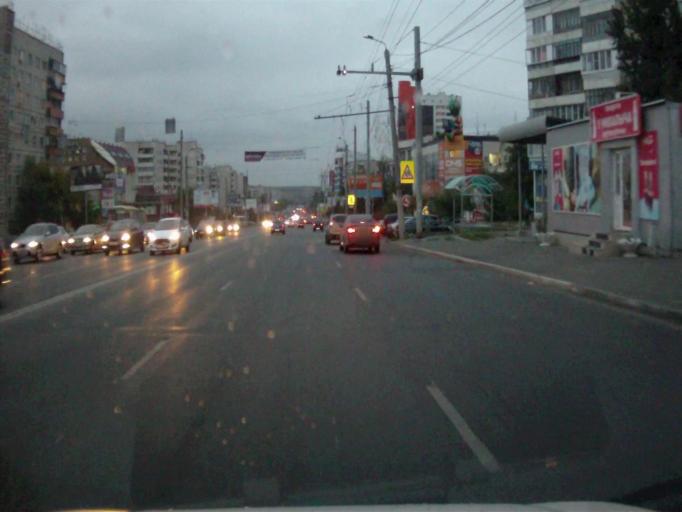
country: RU
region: Chelyabinsk
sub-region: Gorod Chelyabinsk
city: Chelyabinsk
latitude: 55.1882
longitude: 61.3325
